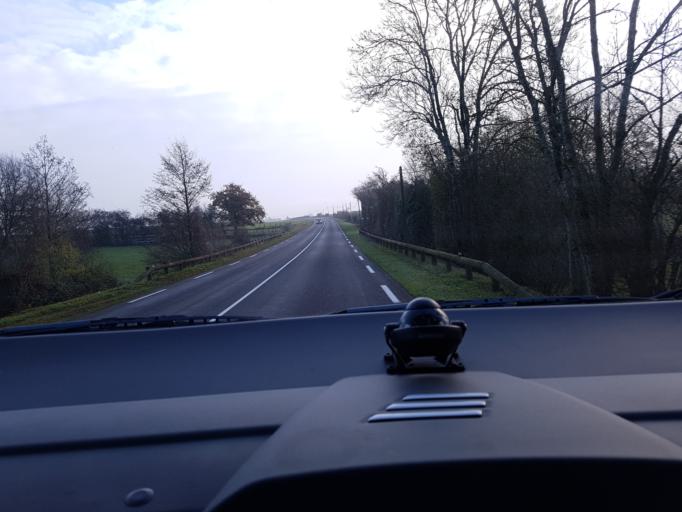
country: FR
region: Lower Normandy
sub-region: Departement de l'Orne
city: Magny-le-Desert
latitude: 48.6289
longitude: -0.2502
